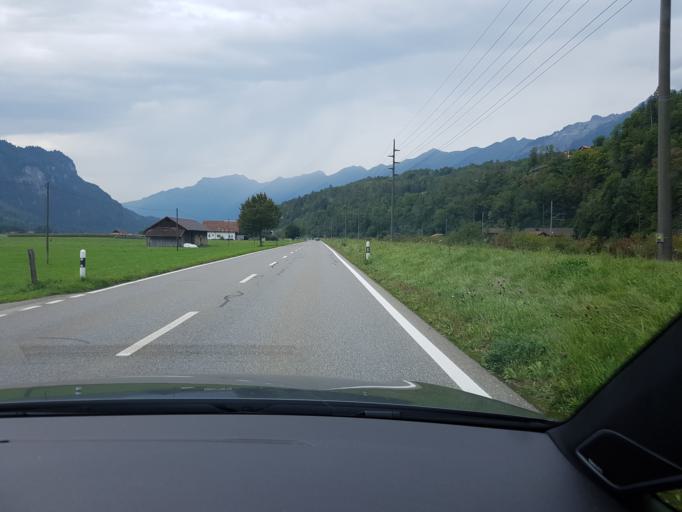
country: CH
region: Obwalden
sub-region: Obwalden
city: Lungern
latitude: 46.7458
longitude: 8.1075
